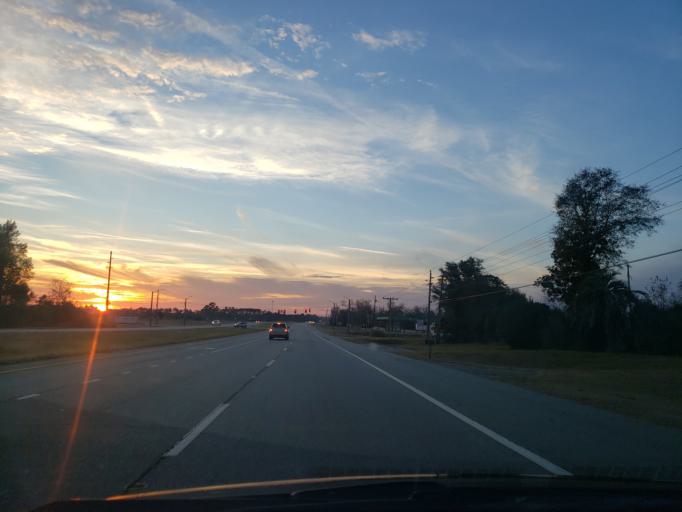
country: US
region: Georgia
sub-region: Dougherty County
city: Albany
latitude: 31.5728
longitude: -84.0501
